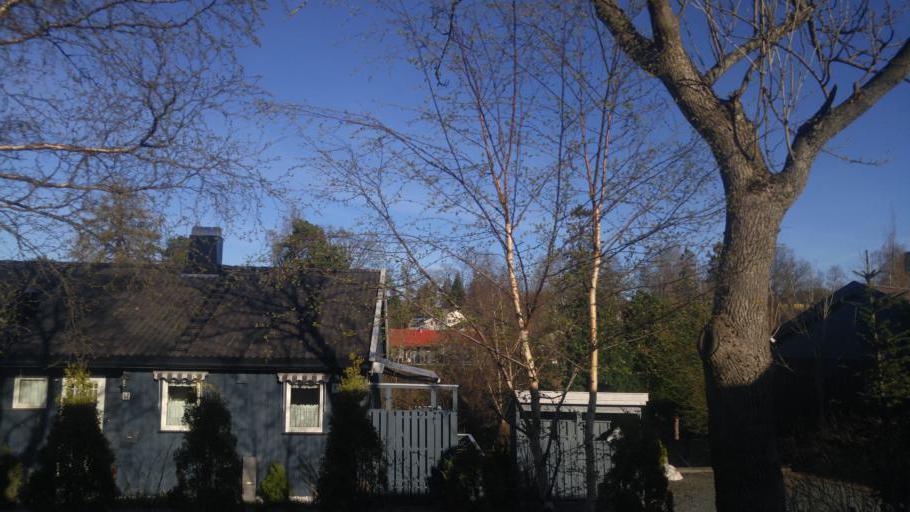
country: NO
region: Sor-Trondelag
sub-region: Trondheim
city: Trondheim
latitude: 63.4261
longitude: 10.4593
